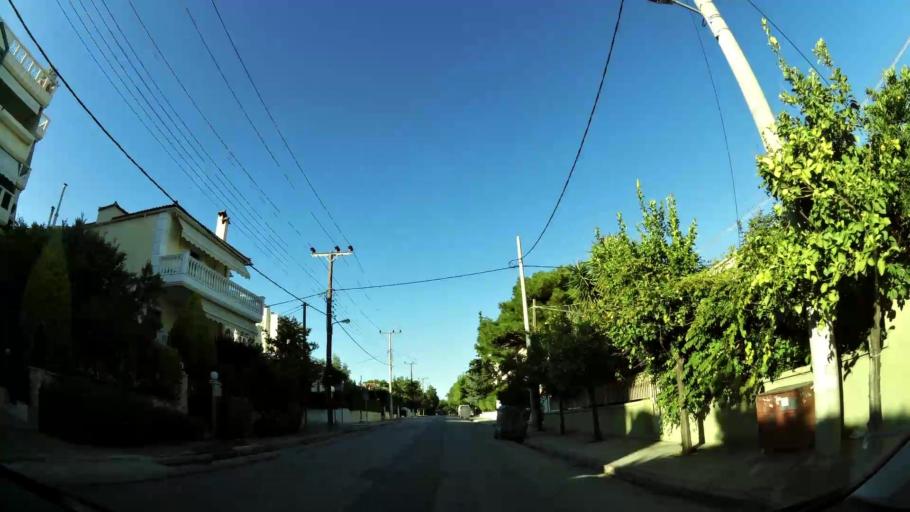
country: GR
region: Attica
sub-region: Nomarchia Anatolikis Attikis
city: Paiania
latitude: 37.9586
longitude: 23.8524
